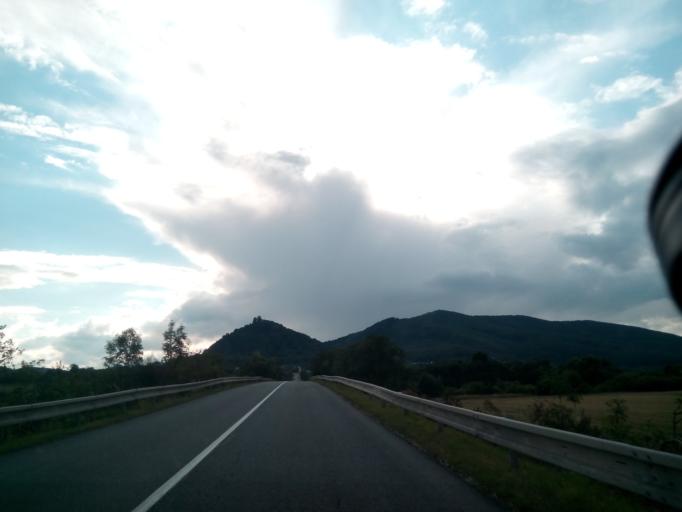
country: SK
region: Kosicky
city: Secovce
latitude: 48.6360
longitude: 21.4927
